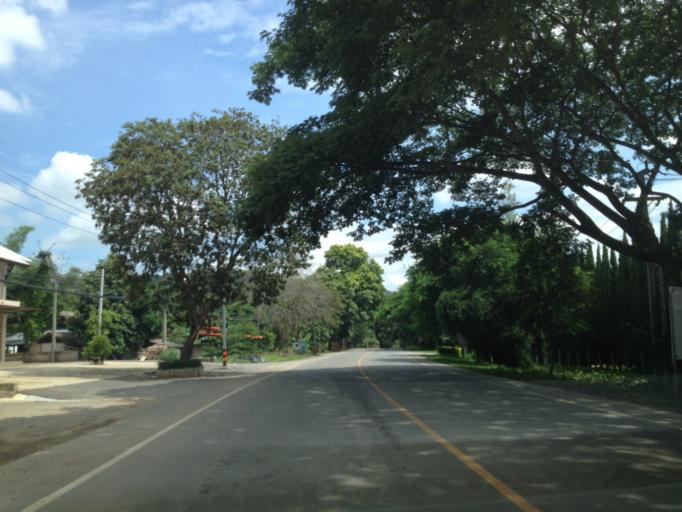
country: TH
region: Chiang Mai
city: Hang Dong
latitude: 18.7492
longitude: 98.8903
